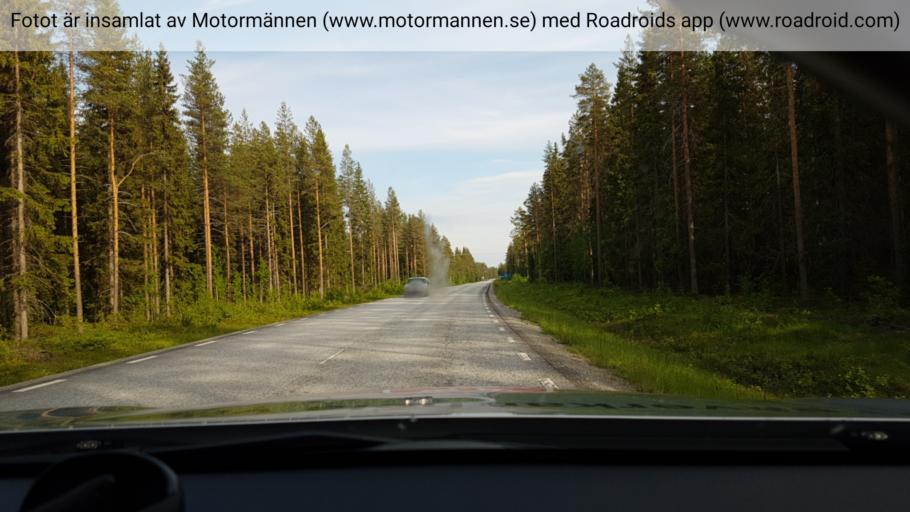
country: SE
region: Vaesterbotten
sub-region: Vindelns Kommun
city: Vindeln
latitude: 64.0897
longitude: 19.6173
